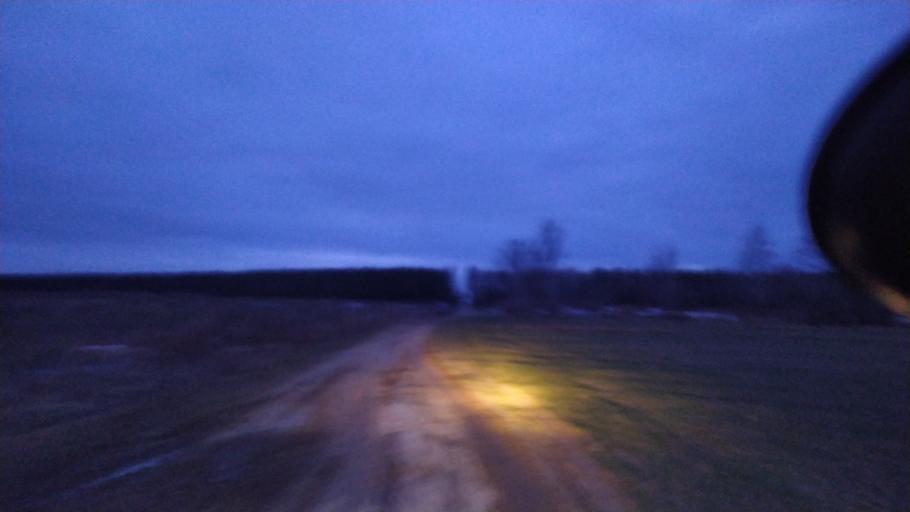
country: PL
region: Lublin Voivodeship
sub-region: Powiat lubelski
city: Jastkow
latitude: 51.3805
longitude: 22.4383
